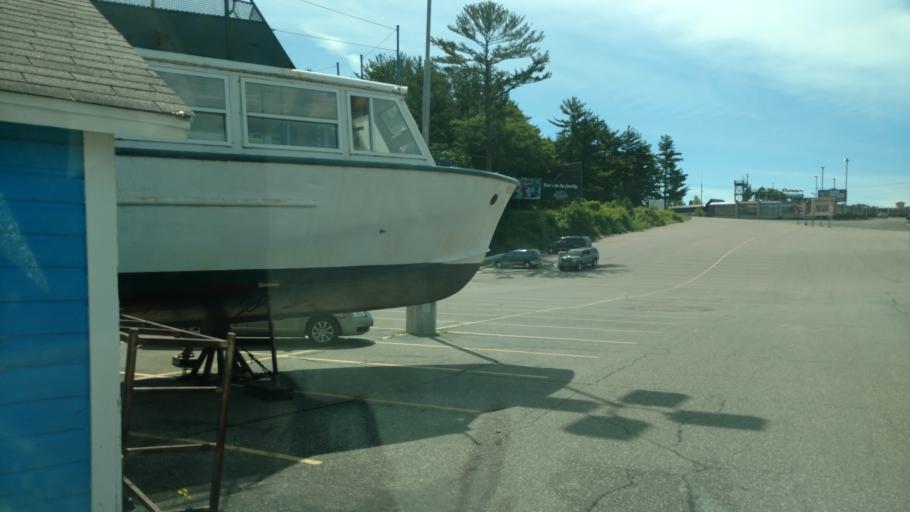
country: US
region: Wisconsin
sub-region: Columbia County
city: Wisconsin Dells
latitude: 43.6246
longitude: -89.7850
